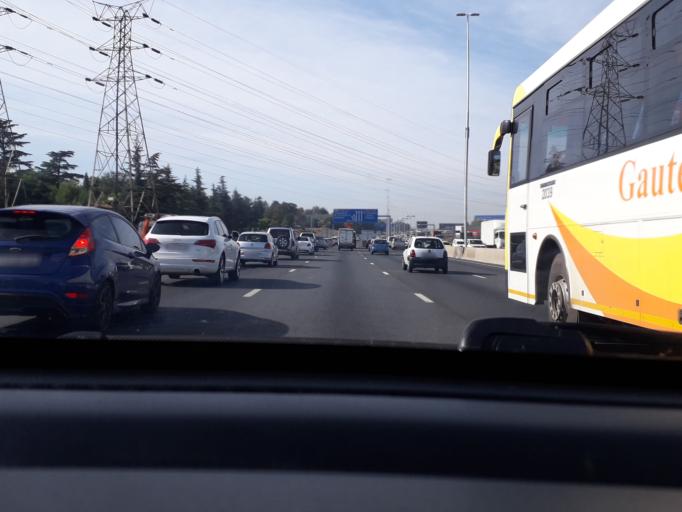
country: ZA
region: Gauteng
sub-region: City of Johannesburg Metropolitan Municipality
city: Modderfontein
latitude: -26.1567
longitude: 28.1332
